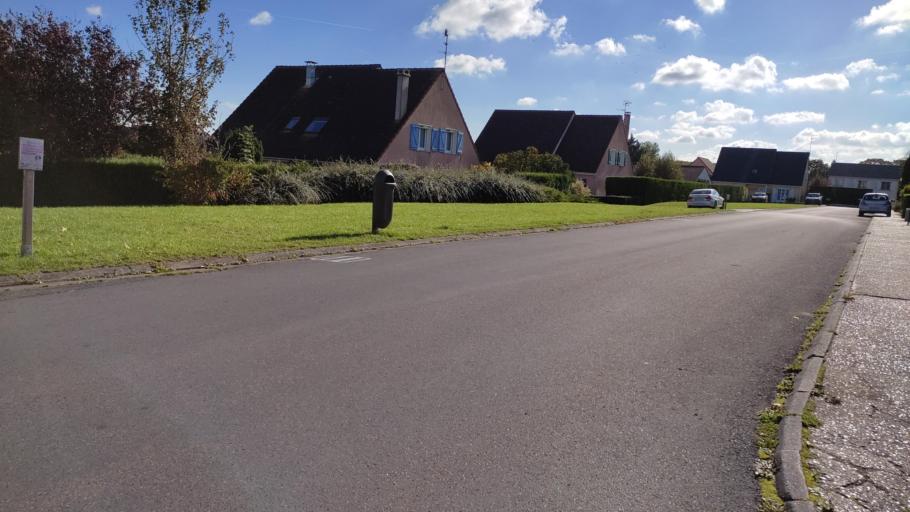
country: FR
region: Nord-Pas-de-Calais
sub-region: Departement du Pas-de-Calais
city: Sainte-Catherine
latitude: 50.3075
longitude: 2.7686
